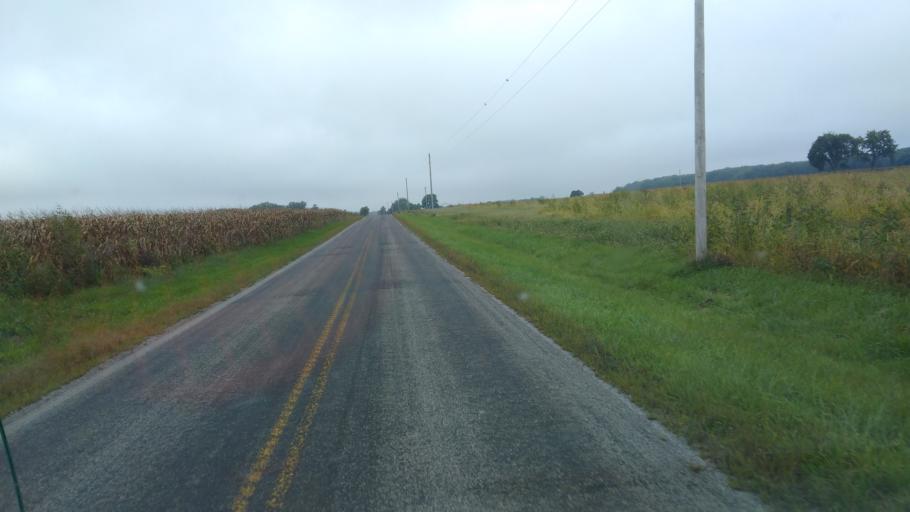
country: US
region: Ohio
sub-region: Hardin County
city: Kenton
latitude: 40.5531
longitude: -83.6354
